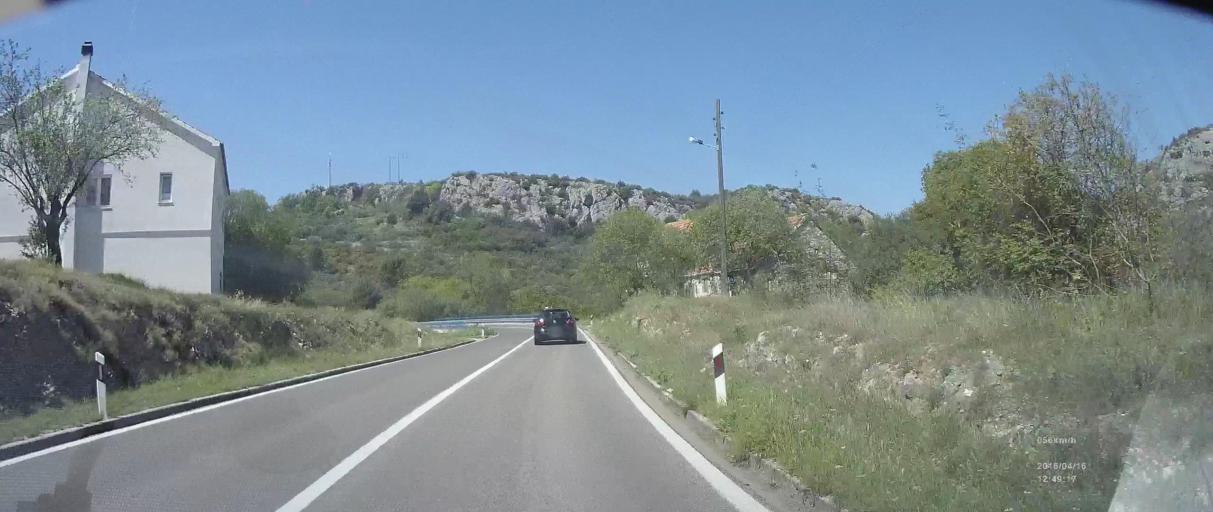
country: HR
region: Sibensko-Kniniska
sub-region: Grad Sibenik
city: Brodarica
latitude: 43.6739
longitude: 16.0280
